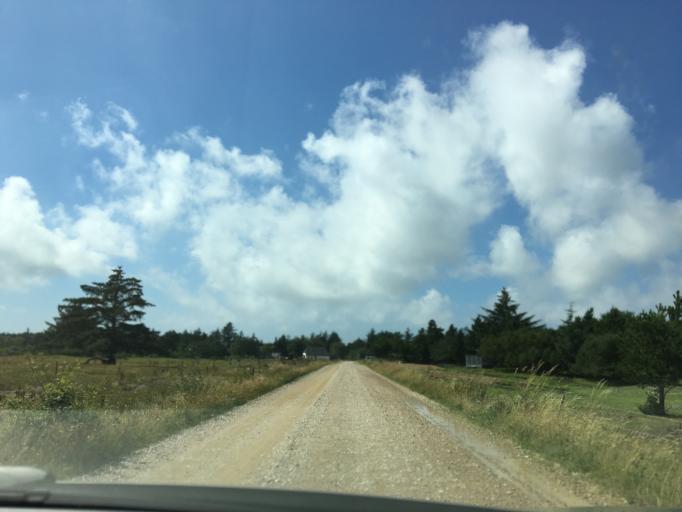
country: DK
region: South Denmark
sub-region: Varde Kommune
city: Oksbol
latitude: 55.7383
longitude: 8.2290
